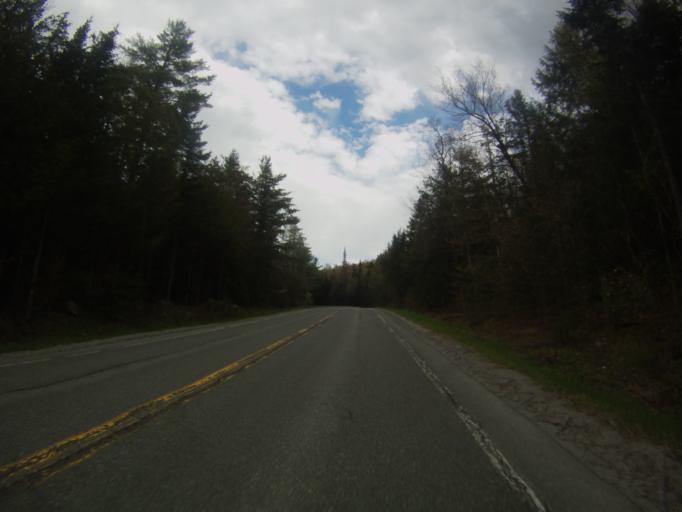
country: US
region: New York
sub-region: Essex County
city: Mineville
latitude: 44.0985
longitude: -73.5654
